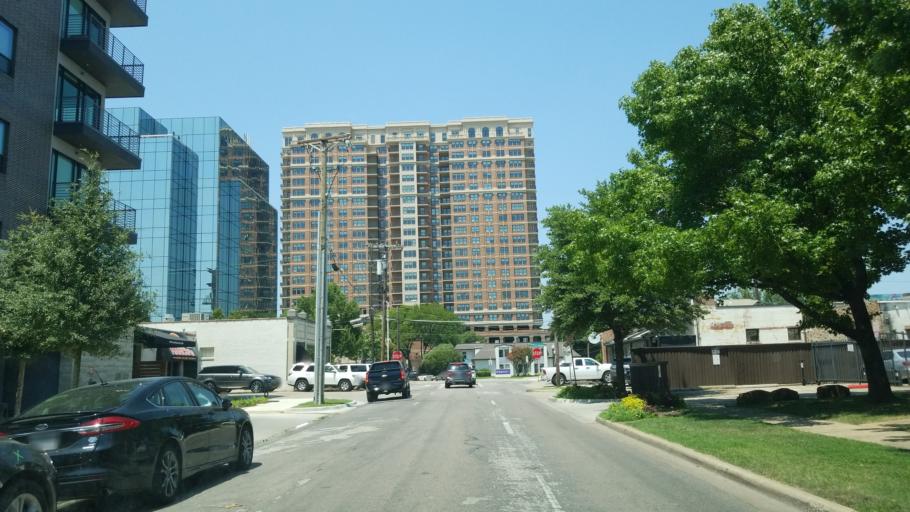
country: US
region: Texas
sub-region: Dallas County
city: Highland Park
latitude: 32.8263
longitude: -96.7857
